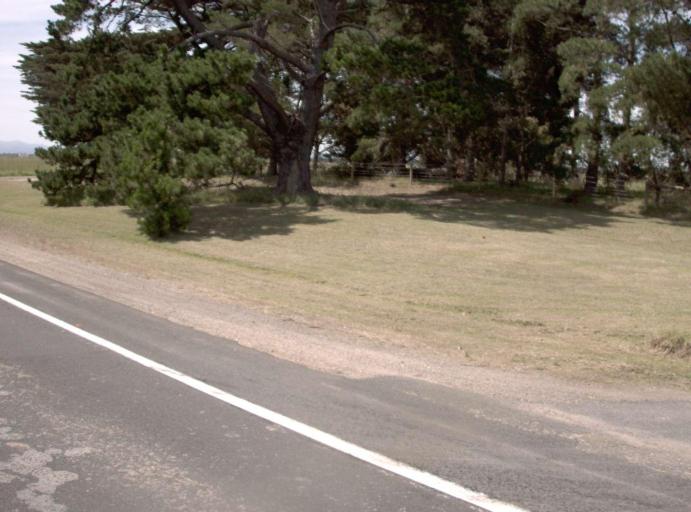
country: AU
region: Victoria
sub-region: Wellington
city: Sale
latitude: -38.0525
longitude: 147.0669
